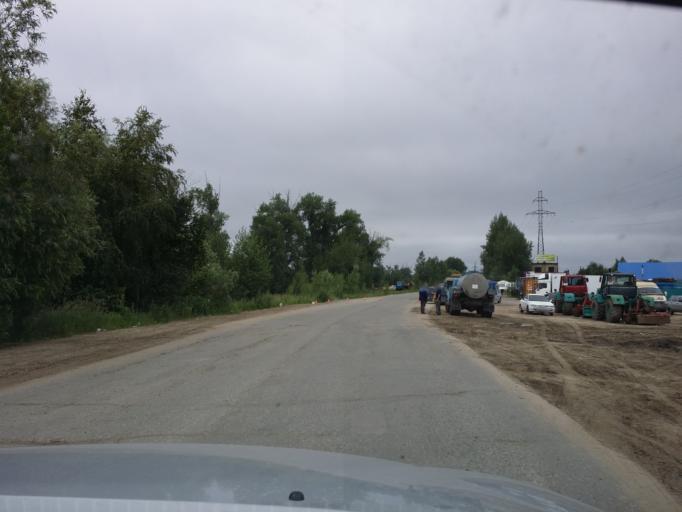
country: RU
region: Khanty-Mansiyskiy Avtonomnyy Okrug
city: Nizhnevartovsk
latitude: 60.8898
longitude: 76.4784
